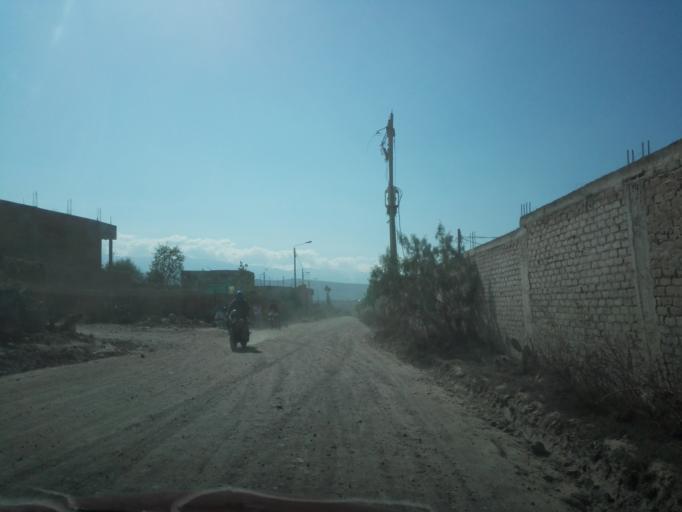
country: PE
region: Ayacucho
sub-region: Provincia de Huamanga
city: Ayacucho
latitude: -13.1598
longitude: -74.2043
